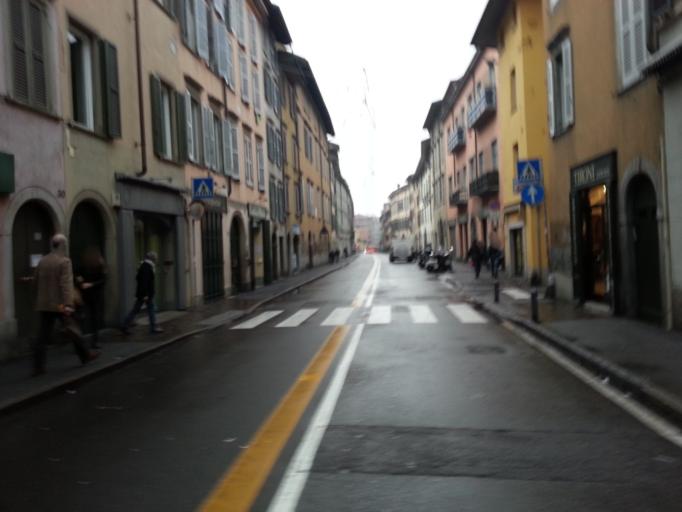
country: IT
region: Lombardy
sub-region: Provincia di Bergamo
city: Bergamo
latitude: 45.6929
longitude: 9.6620
